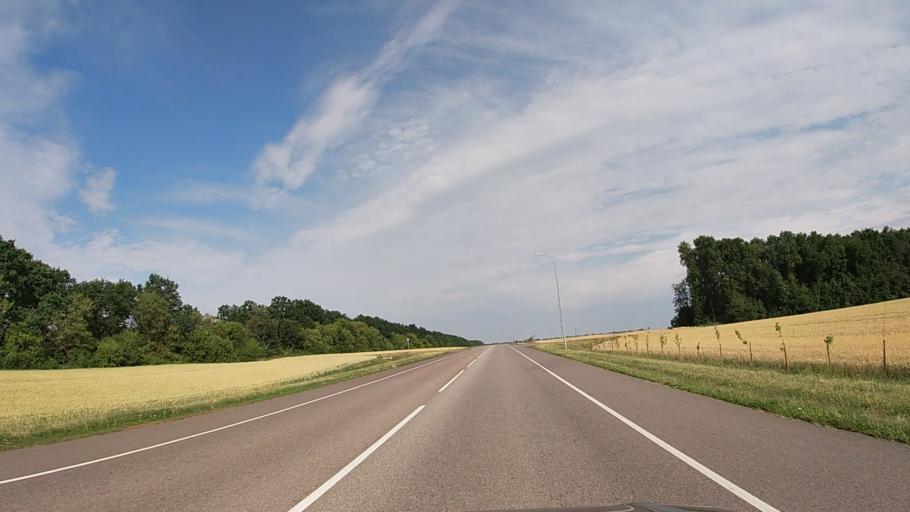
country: RU
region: Belgorod
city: Proletarskiy
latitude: 50.8245
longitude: 35.7832
